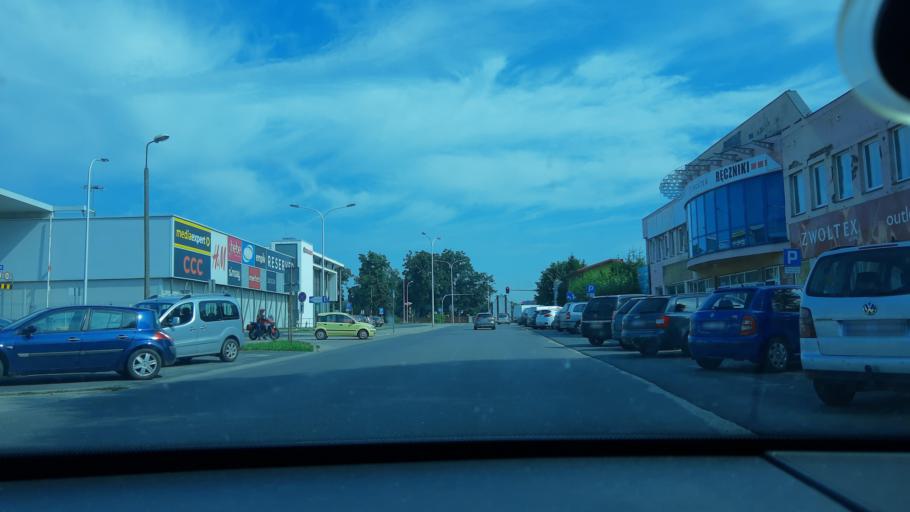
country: PL
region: Lodz Voivodeship
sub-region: Powiat sieradzki
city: Sieradz
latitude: 51.5963
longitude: 18.7264
